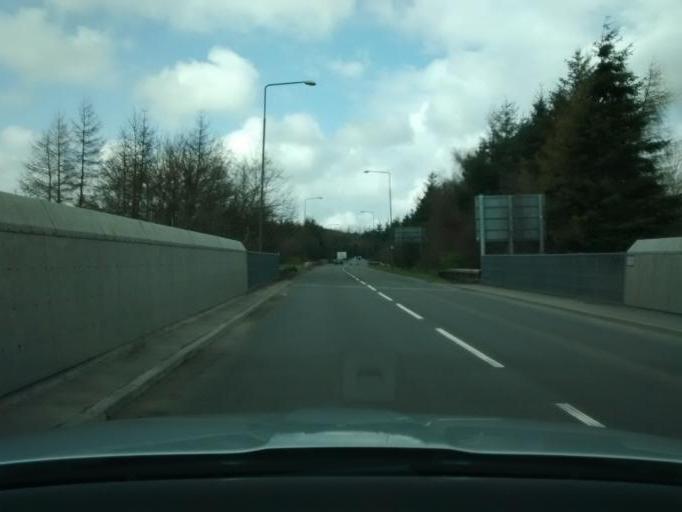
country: GB
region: Scotland
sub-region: West Lothian
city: Livingston
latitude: 55.8962
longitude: -3.5661
